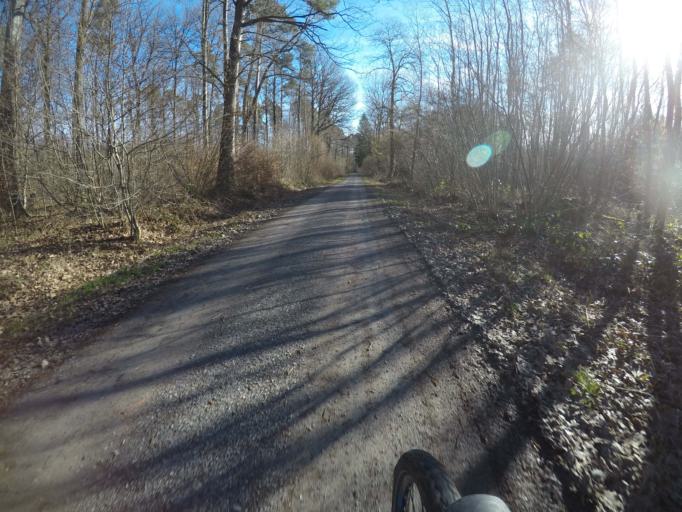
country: DE
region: Baden-Wuerttemberg
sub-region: Regierungsbezirk Stuttgart
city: Steinenbronn
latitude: 48.6902
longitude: 9.1042
